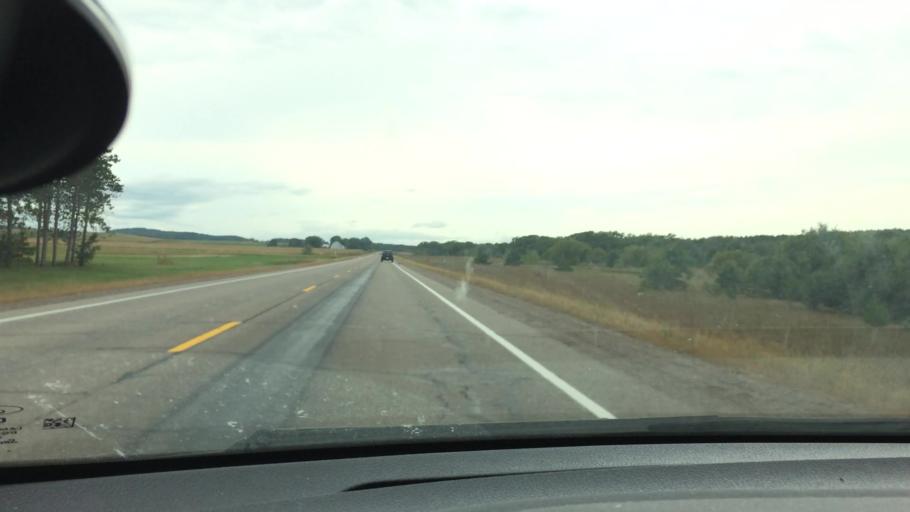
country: US
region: Wisconsin
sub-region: Eau Claire County
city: Augusta
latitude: 44.5858
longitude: -91.1262
